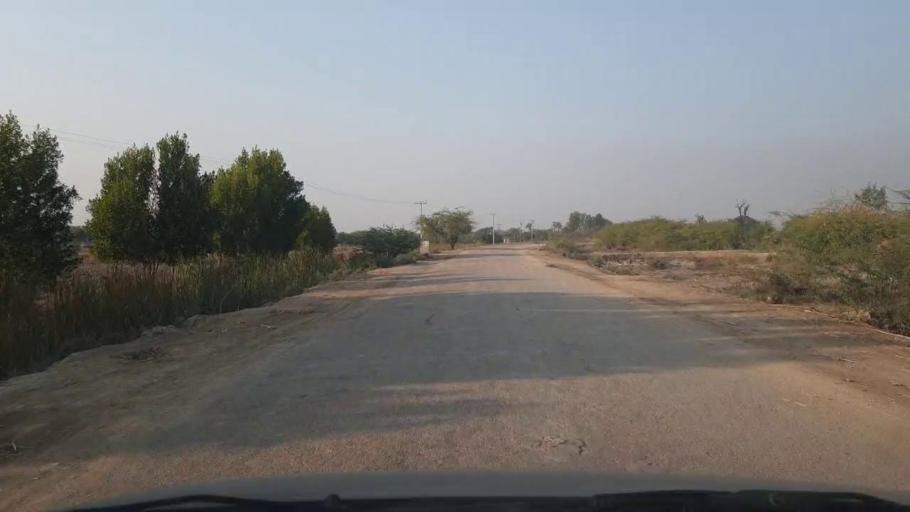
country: PK
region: Sindh
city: Mirwah Gorchani
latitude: 25.3246
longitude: 69.1652
